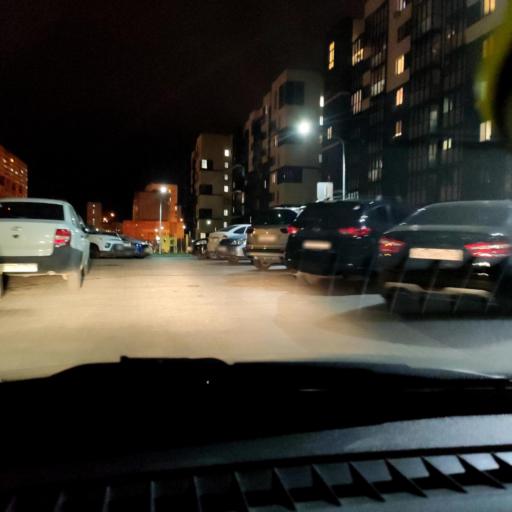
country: RU
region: Samara
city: Tol'yatti
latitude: 53.5260
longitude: 49.3392
